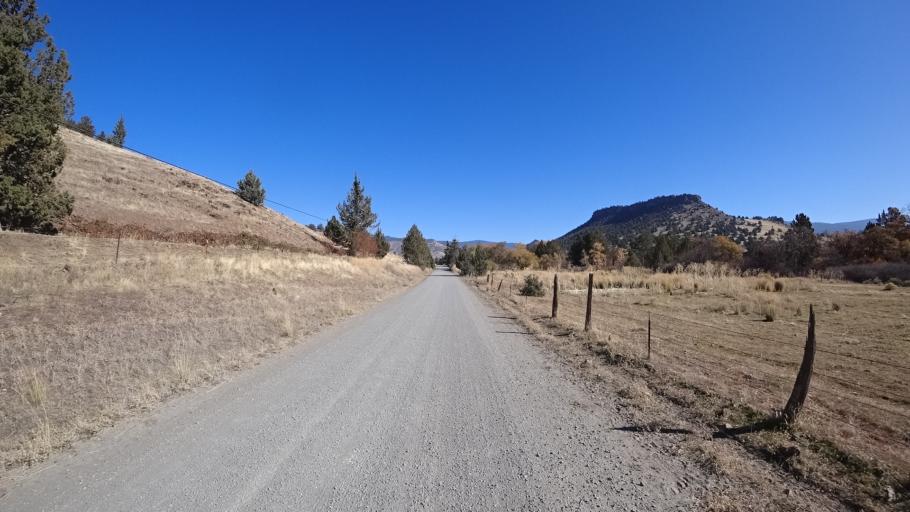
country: US
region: California
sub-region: Siskiyou County
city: Montague
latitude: 41.7314
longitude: -122.3550
